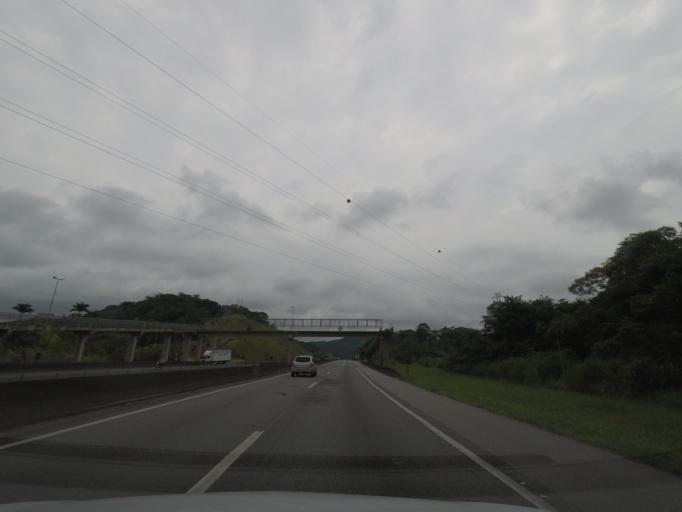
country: BR
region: Sao Paulo
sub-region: Juquia
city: Juquia
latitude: -24.3486
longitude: -47.6514
